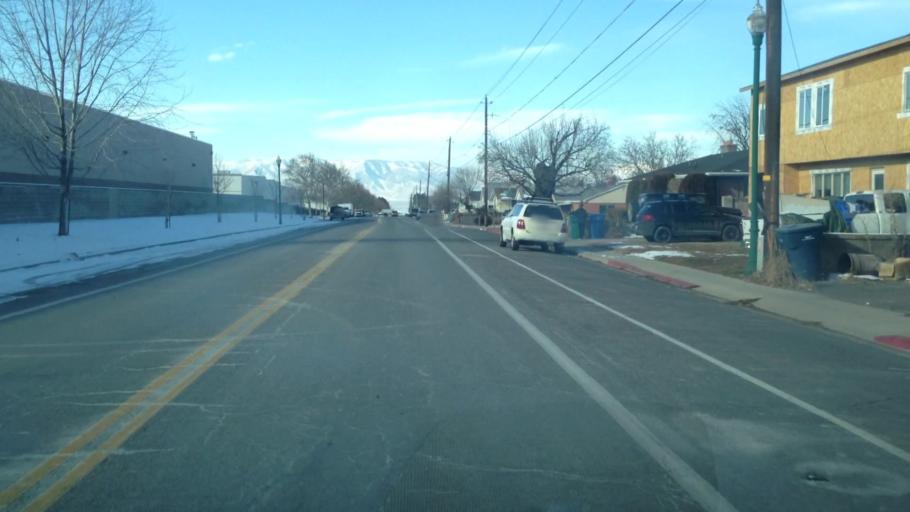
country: US
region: Utah
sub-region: Utah County
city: Orem
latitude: 40.2753
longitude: -111.6980
